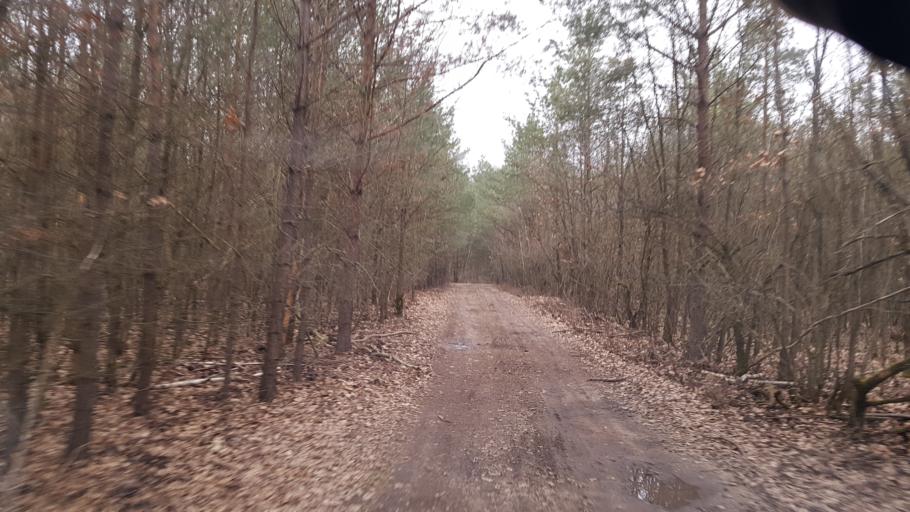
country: DE
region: Brandenburg
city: Trobitz
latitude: 51.6129
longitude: 13.4561
